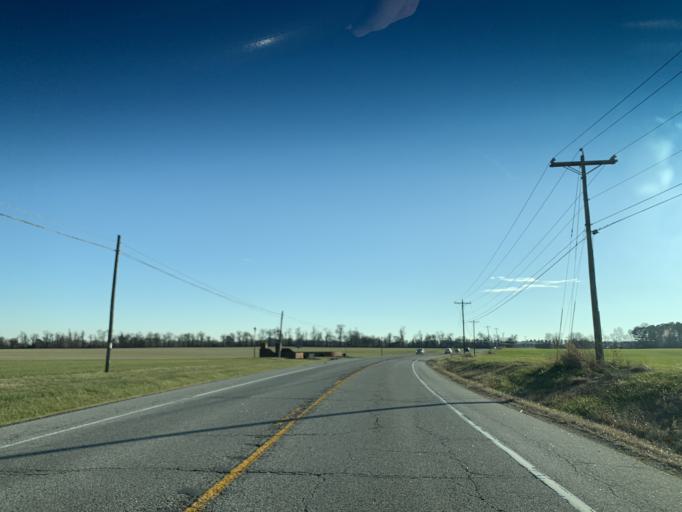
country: US
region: Delaware
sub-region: New Castle County
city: Middletown
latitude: 39.3905
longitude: -75.8712
